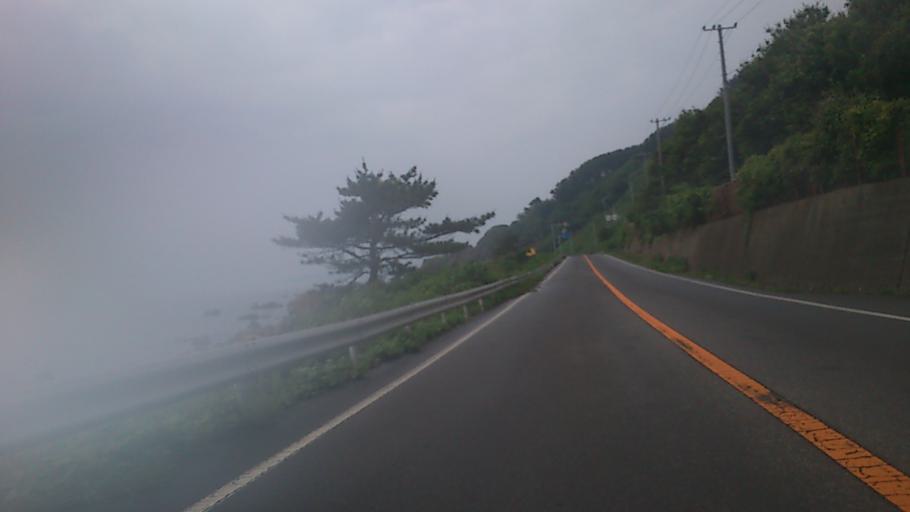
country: JP
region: Akita
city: Noshiromachi
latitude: 40.4401
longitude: 139.9402
